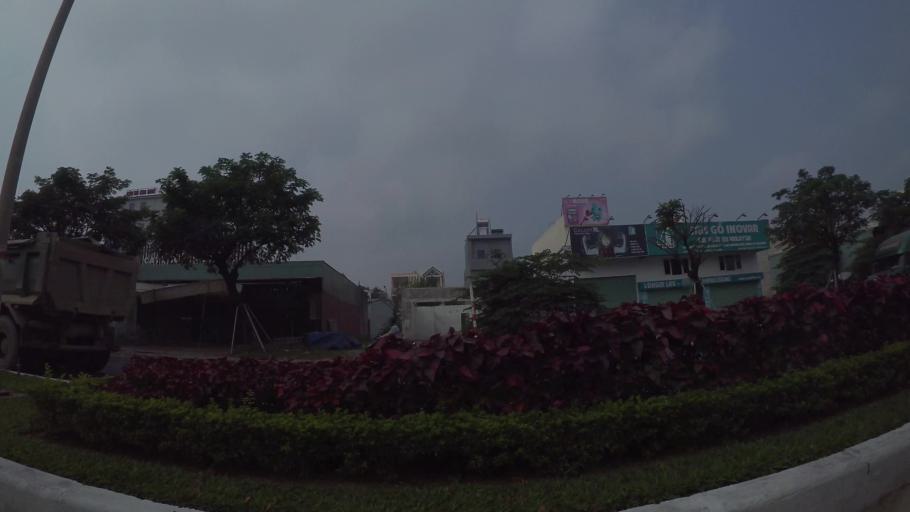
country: VN
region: Da Nang
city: Cam Le
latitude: 16.0096
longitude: 108.2182
